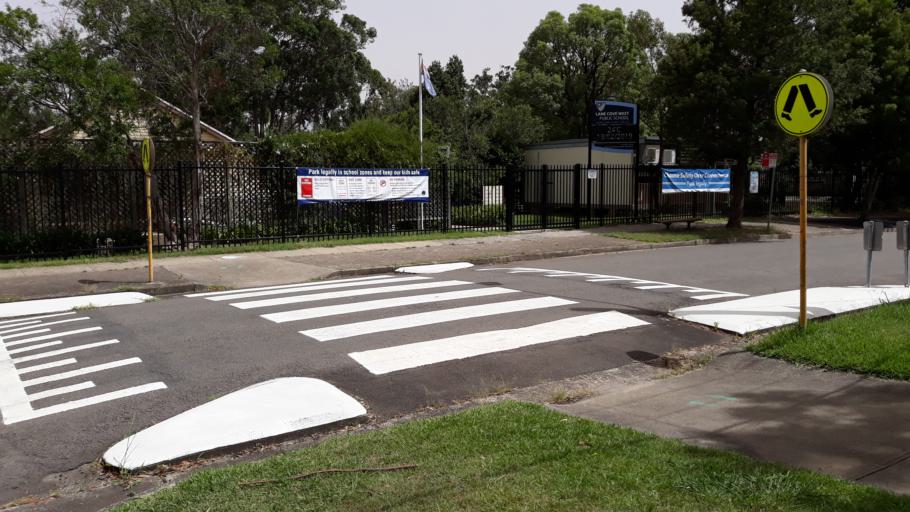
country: AU
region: New South Wales
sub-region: Lane Cove
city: Lane Cove West
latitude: -33.8105
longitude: 151.1531
